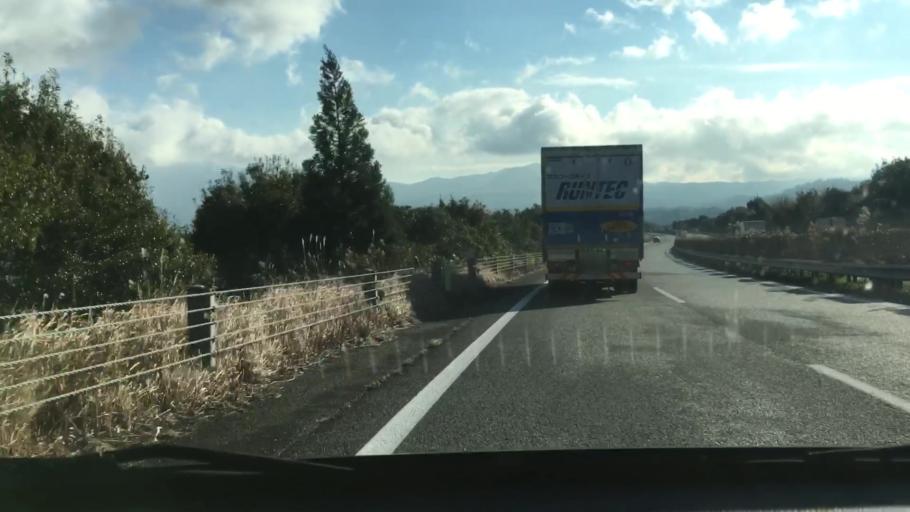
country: JP
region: Kumamoto
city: Hitoyoshi
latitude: 32.0611
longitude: 130.8038
